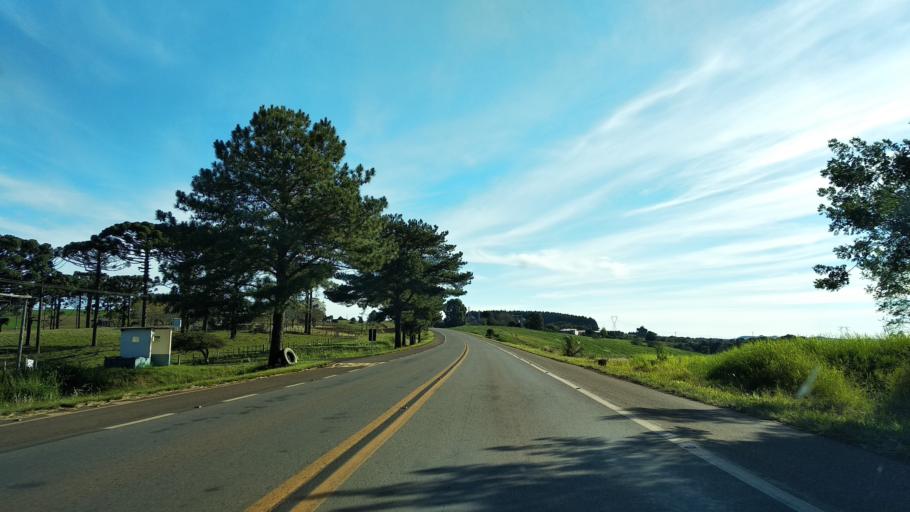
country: BR
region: Santa Catarina
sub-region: Celso Ramos
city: Celso Ramos
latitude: -27.5269
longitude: -51.3746
